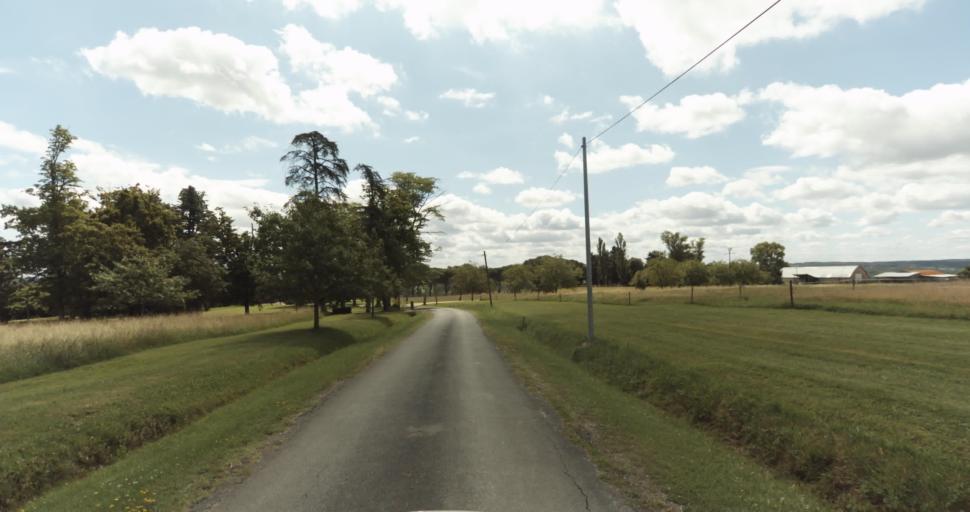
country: FR
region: Aquitaine
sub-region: Departement de la Gironde
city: Bazas
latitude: 44.4585
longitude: -0.1751
